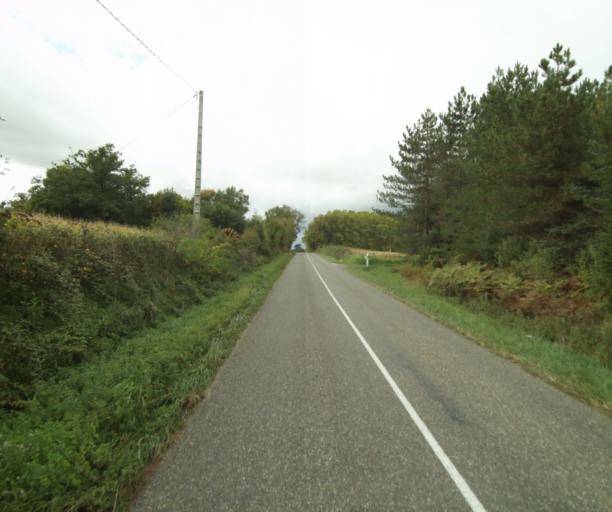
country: FR
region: Midi-Pyrenees
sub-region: Departement du Gers
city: Eauze
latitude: 43.8600
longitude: 0.0390
